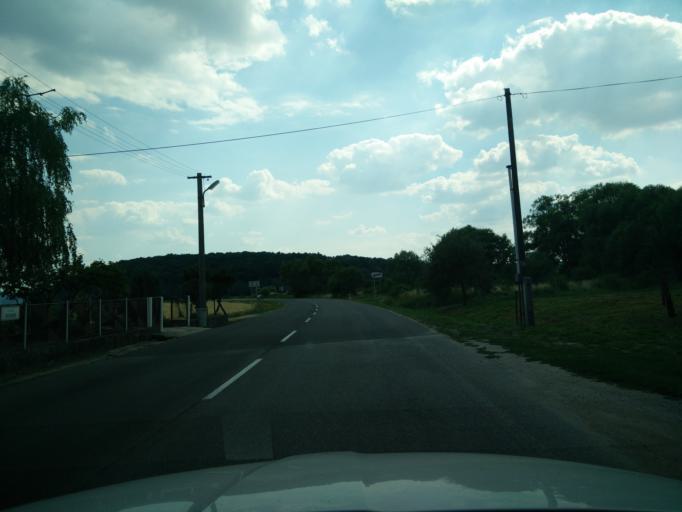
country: SK
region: Nitriansky
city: Partizanske
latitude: 48.6782
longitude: 18.3701
